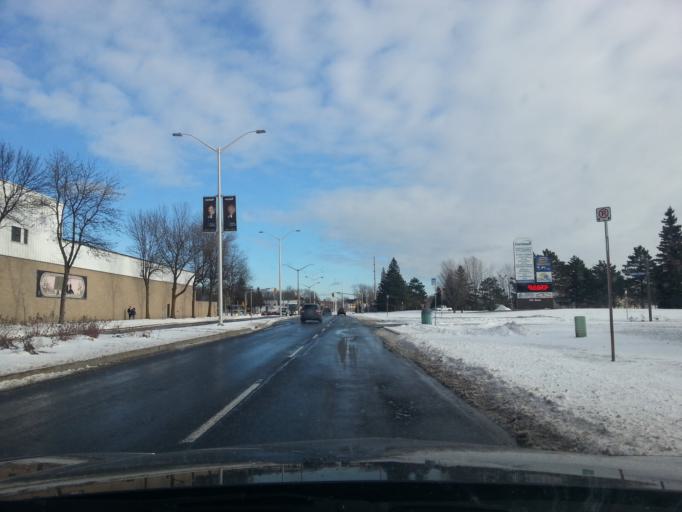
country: CA
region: Ontario
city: Cornwall
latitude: 45.0156
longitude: -74.7254
